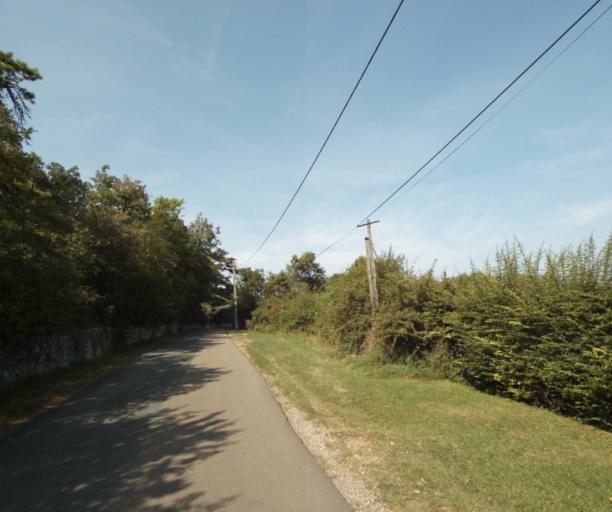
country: FR
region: Bourgogne
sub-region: Departement de Saone-et-Loire
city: Tournus
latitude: 46.5744
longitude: 4.8902
